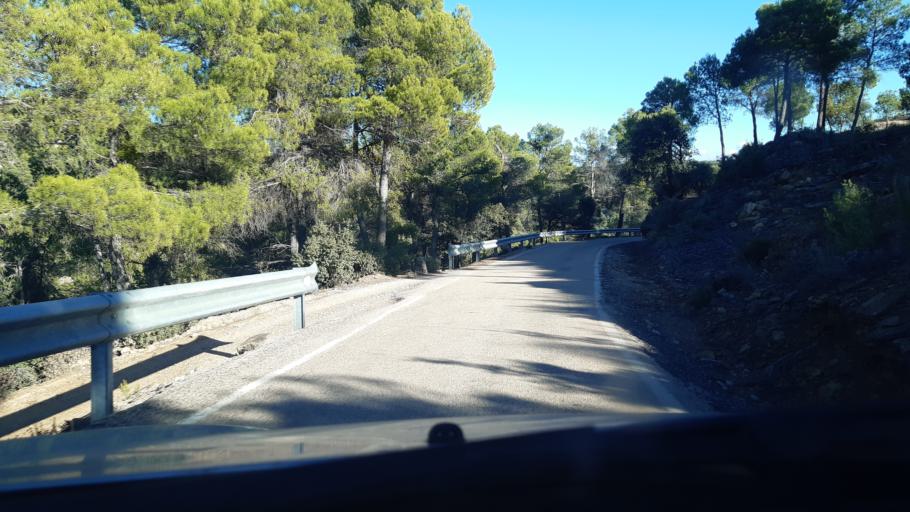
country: ES
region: Aragon
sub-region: Provincia de Teruel
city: Fornoles
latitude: 40.9042
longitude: -0.0067
